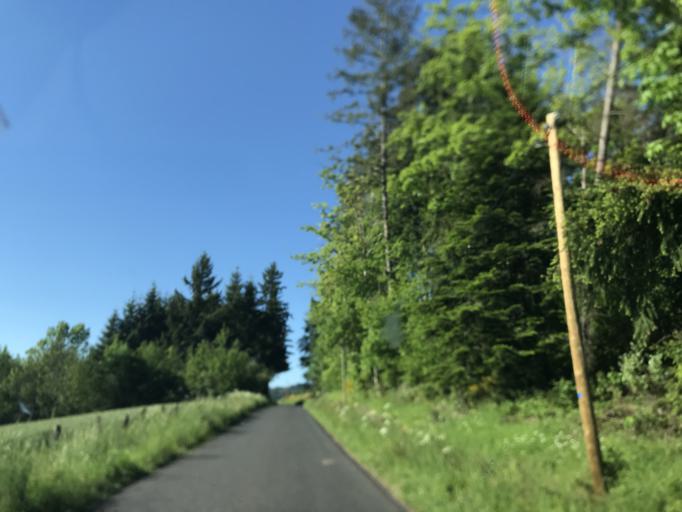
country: FR
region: Auvergne
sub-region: Departement du Puy-de-Dome
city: Job
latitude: 45.6240
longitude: 3.6783
